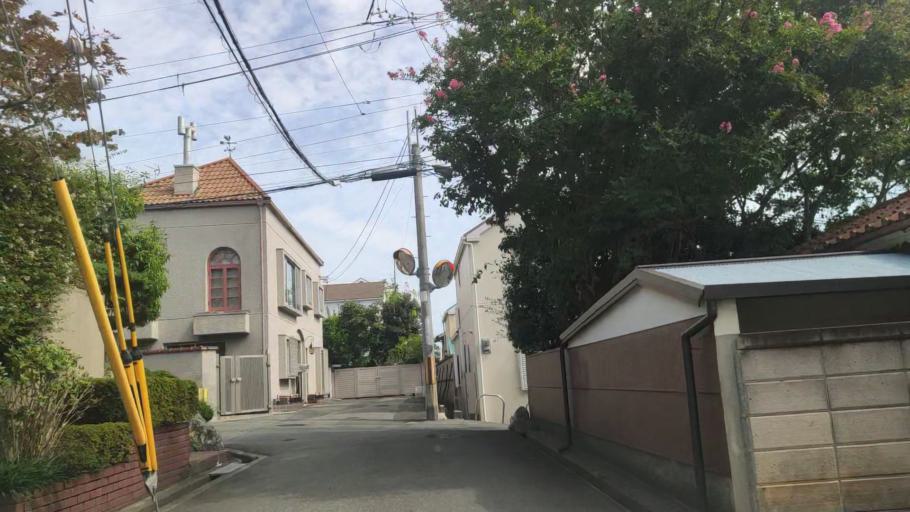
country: JP
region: Osaka
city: Mino
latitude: 34.8143
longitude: 135.4652
